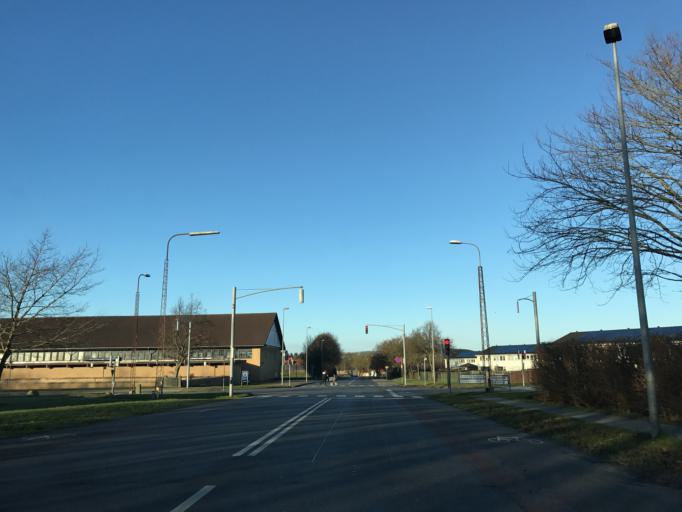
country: DK
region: South Denmark
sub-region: Haderslev Kommune
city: Haderslev
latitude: 55.2321
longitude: 9.4934
